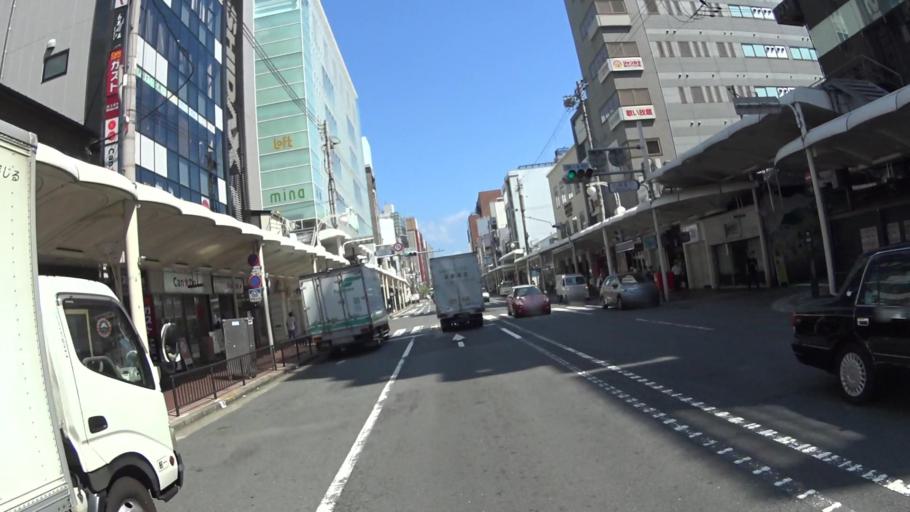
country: JP
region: Kyoto
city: Kyoto
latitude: 35.0064
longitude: 135.7695
